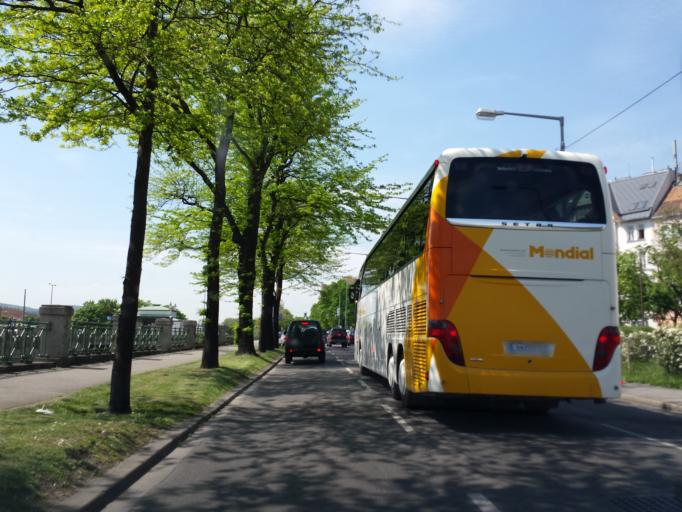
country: AT
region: Vienna
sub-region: Wien Stadt
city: Vienna
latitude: 48.1856
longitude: 16.3221
